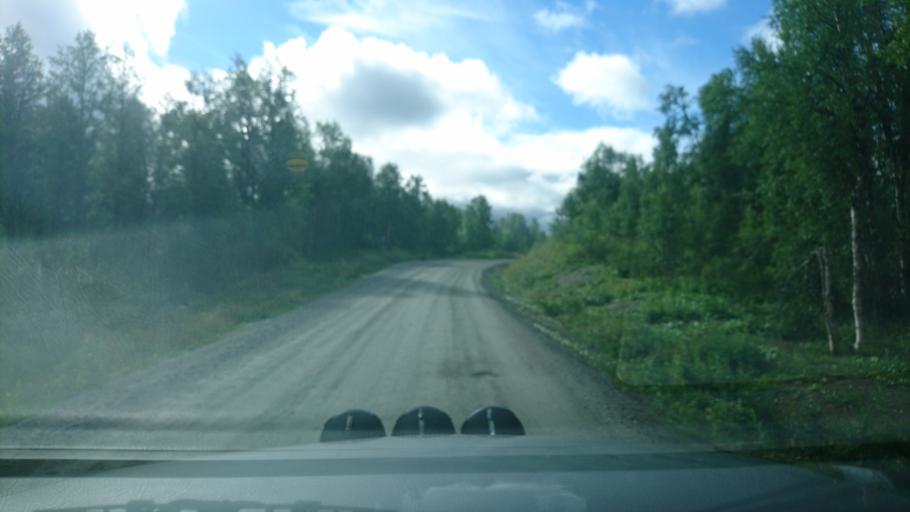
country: NO
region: Nordland
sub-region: Hattfjelldal
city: Hattfjelldal
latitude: 65.7106
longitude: 15.0982
